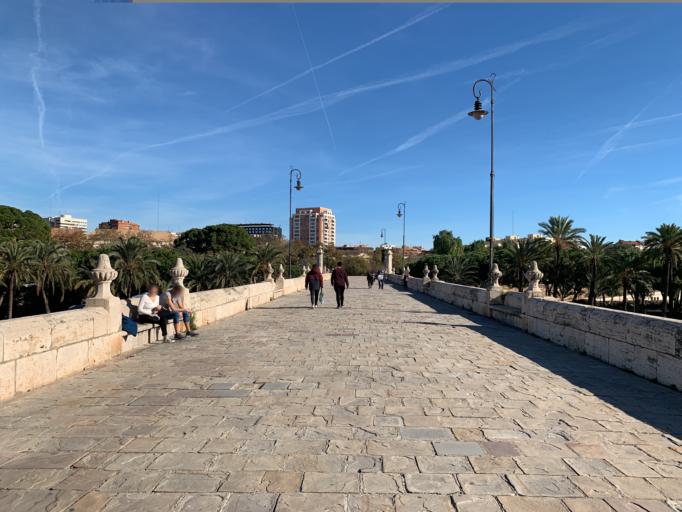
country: ES
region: Valencia
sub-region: Provincia de Valencia
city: Valencia
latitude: 39.4703
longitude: -0.3641
